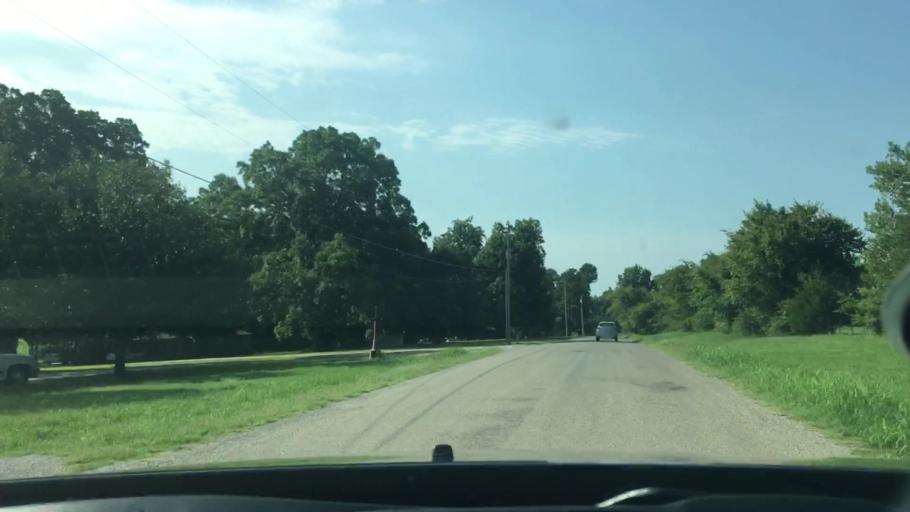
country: US
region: Oklahoma
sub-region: Johnston County
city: Tishomingo
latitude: 34.2201
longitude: -96.6711
